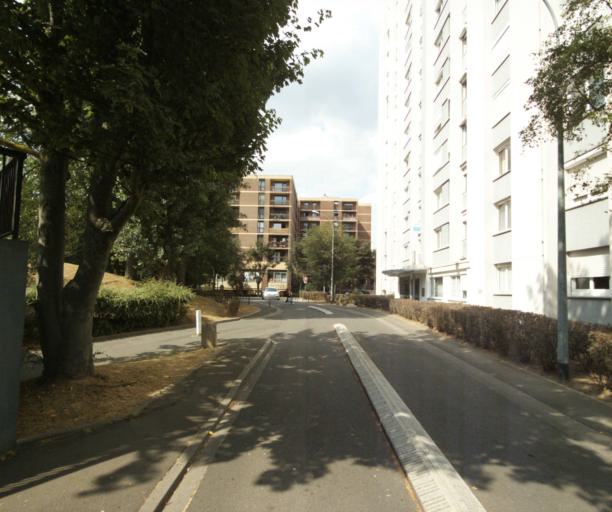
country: FR
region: Nord-Pas-de-Calais
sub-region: Departement du Nord
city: La Madeleine
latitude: 50.6505
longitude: 3.0678
